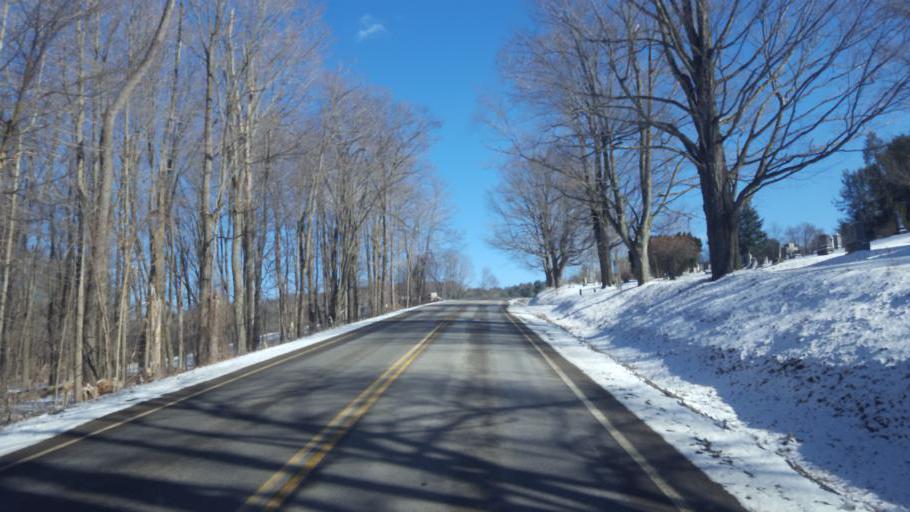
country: US
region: New York
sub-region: Allegany County
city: Friendship
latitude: 42.2054
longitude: -78.1212
